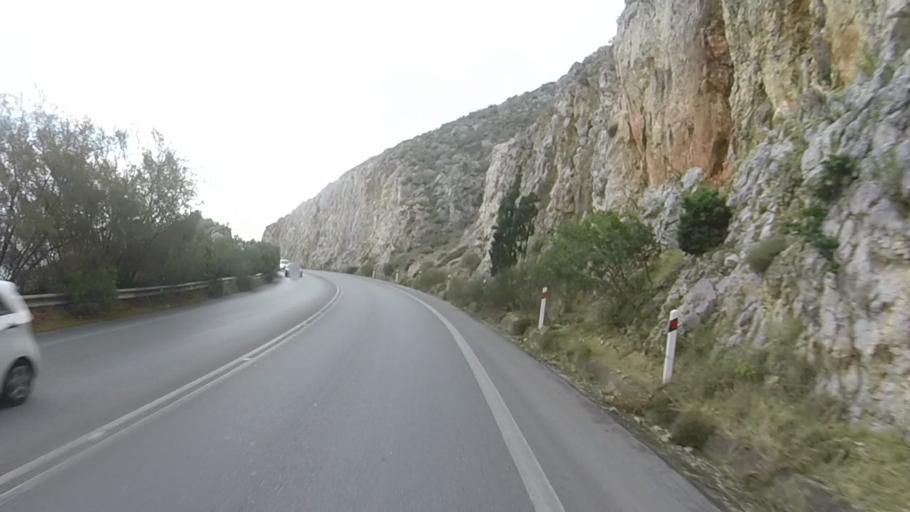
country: GR
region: Crete
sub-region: Nomos Rethymnis
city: Atsipopoulon
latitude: 35.3602
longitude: 24.3792
